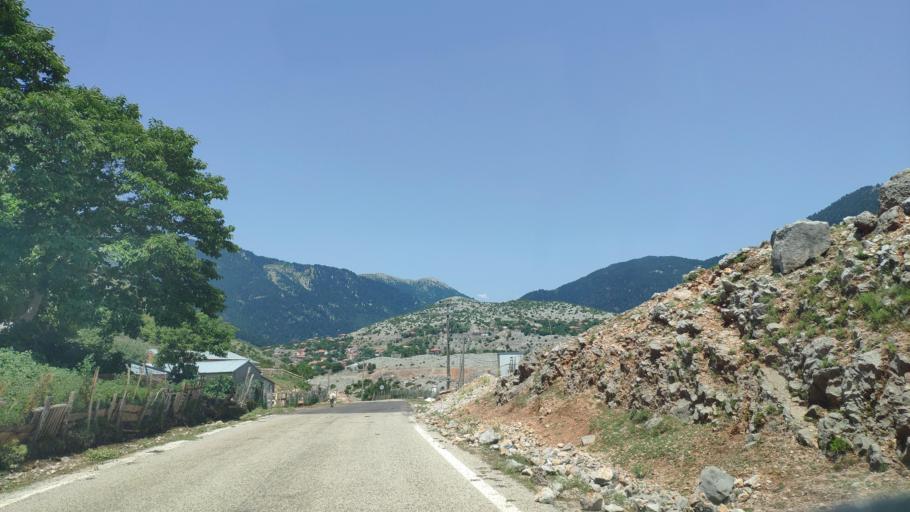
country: GR
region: West Greece
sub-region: Nomos Aitolias kai Akarnanias
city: Krikellos
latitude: 39.0436
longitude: 21.3744
